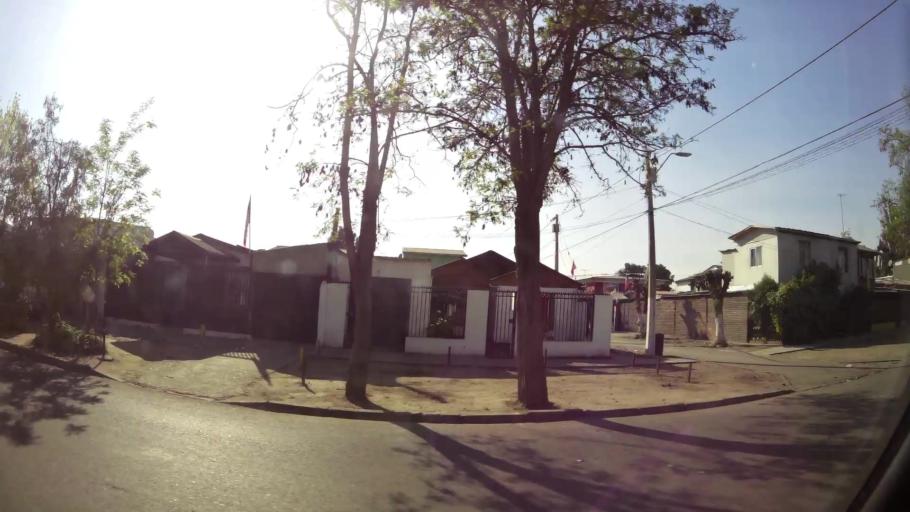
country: CL
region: Santiago Metropolitan
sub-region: Provincia de Santiago
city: Lo Prado
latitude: -33.4196
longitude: -70.7475
